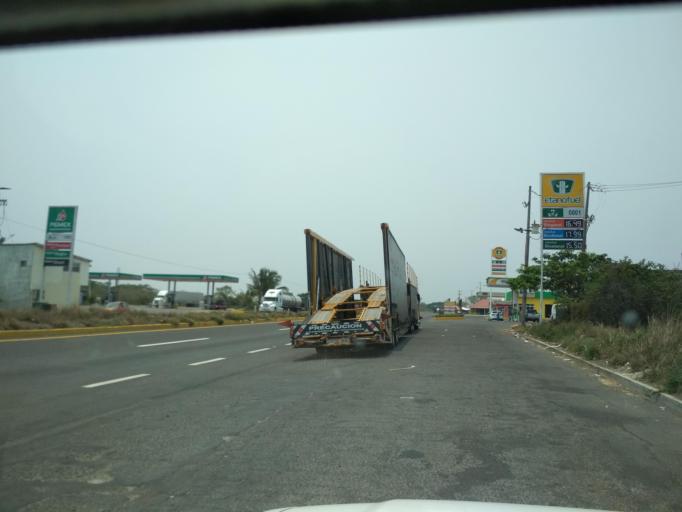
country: MX
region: Veracruz
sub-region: Veracruz
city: Delfino Victoria (Santa Fe)
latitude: 19.2196
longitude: -96.2582
